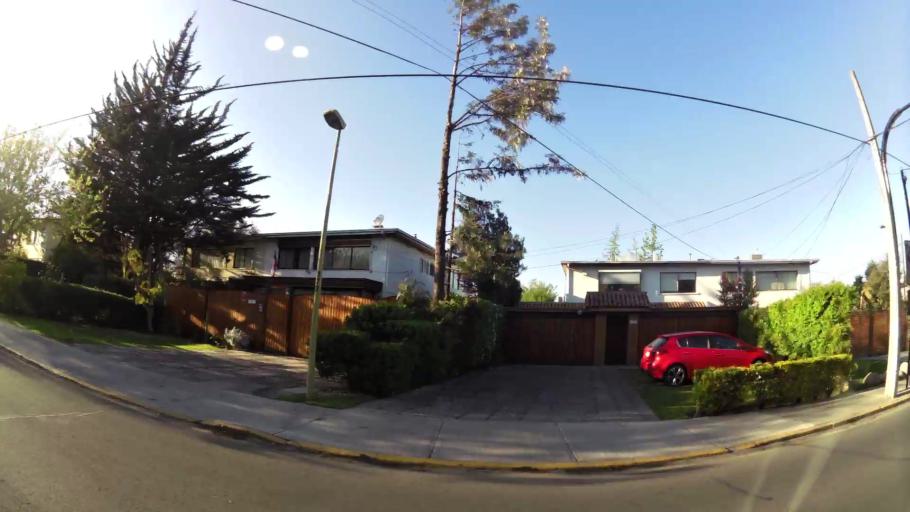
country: CL
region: Santiago Metropolitan
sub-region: Provincia de Santiago
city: Villa Presidente Frei, Nunoa, Santiago, Chile
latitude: -33.3959
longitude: -70.5562
